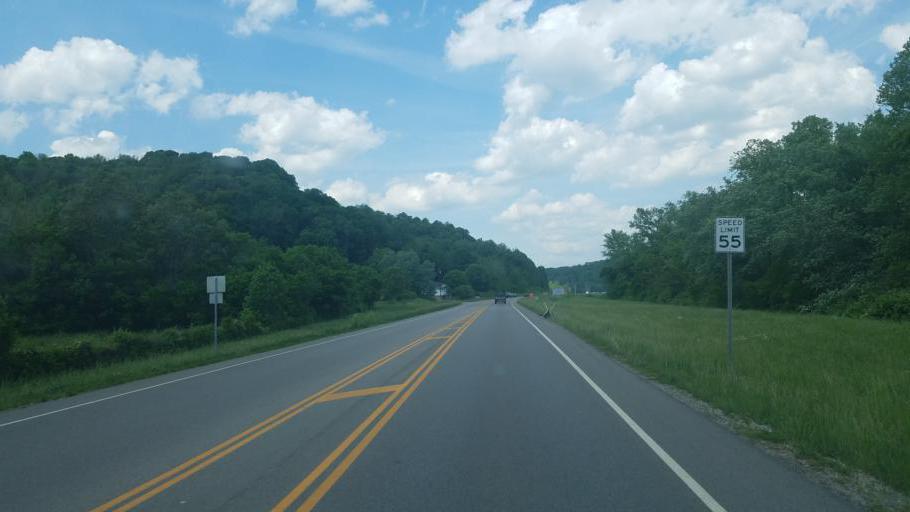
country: US
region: Ohio
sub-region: Meigs County
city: Middleport
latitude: 39.0266
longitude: -82.0660
